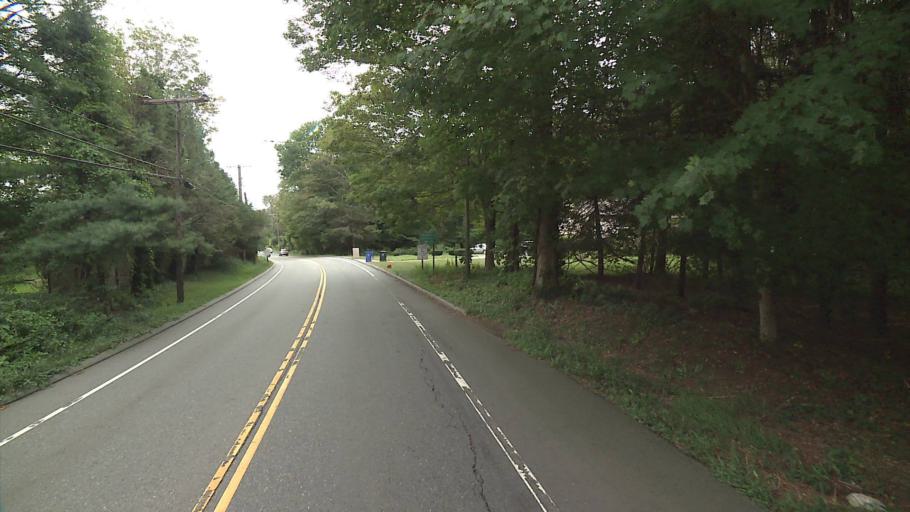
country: US
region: Connecticut
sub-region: New London County
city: Colchester
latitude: 41.5997
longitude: -72.3434
